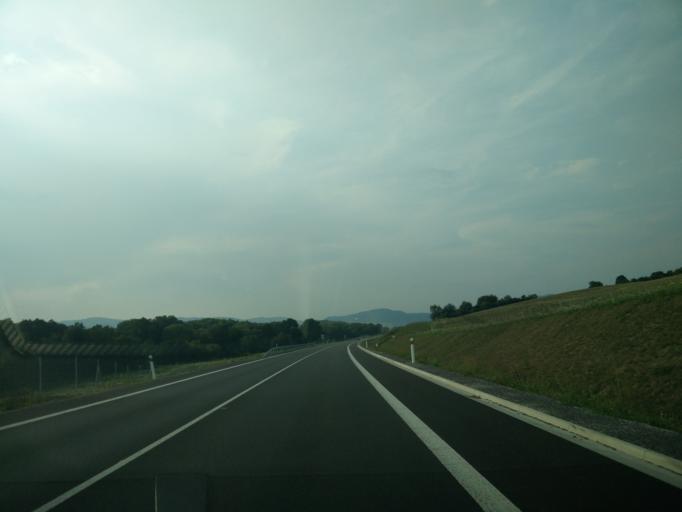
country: SK
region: Banskobystricky
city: Ziar nad Hronom
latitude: 48.5947
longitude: 18.8239
